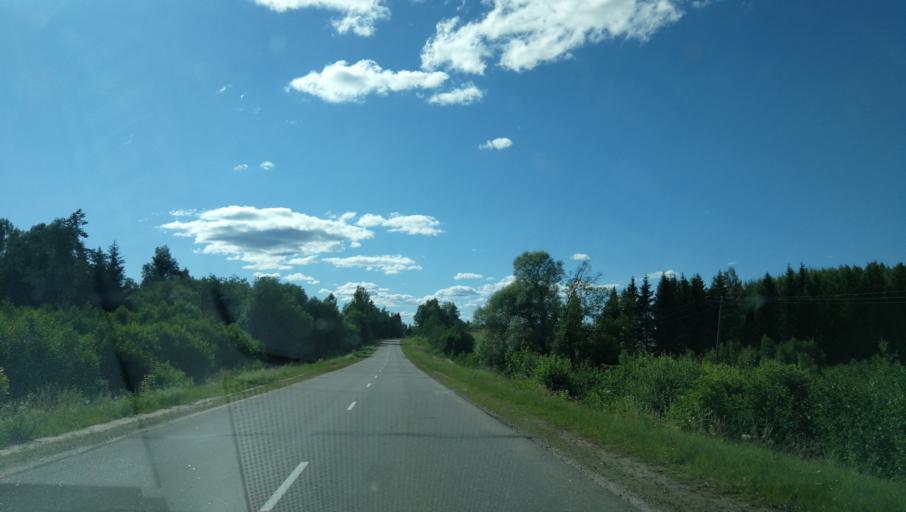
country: LV
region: Madonas Rajons
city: Madona
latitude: 56.8819
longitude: 26.1666
